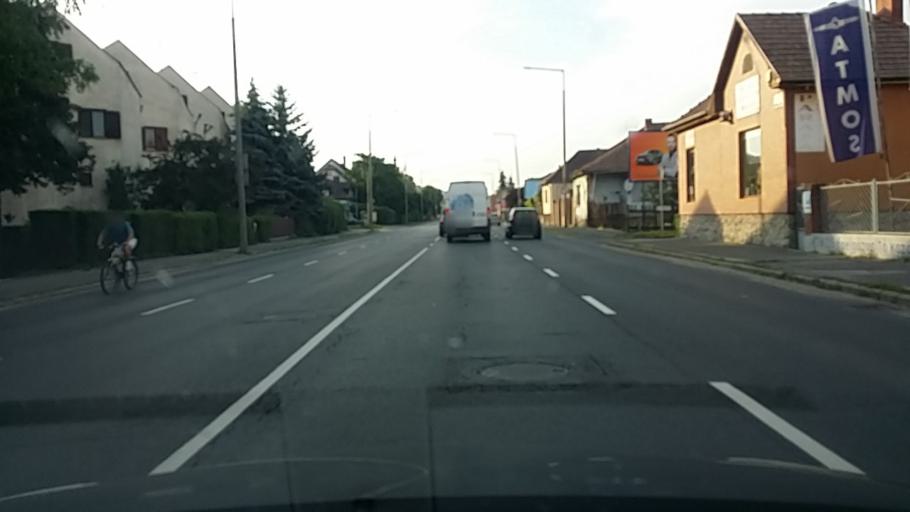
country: HU
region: Borsod-Abauj-Zemplen
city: Miskolc
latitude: 48.0687
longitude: 20.7912
